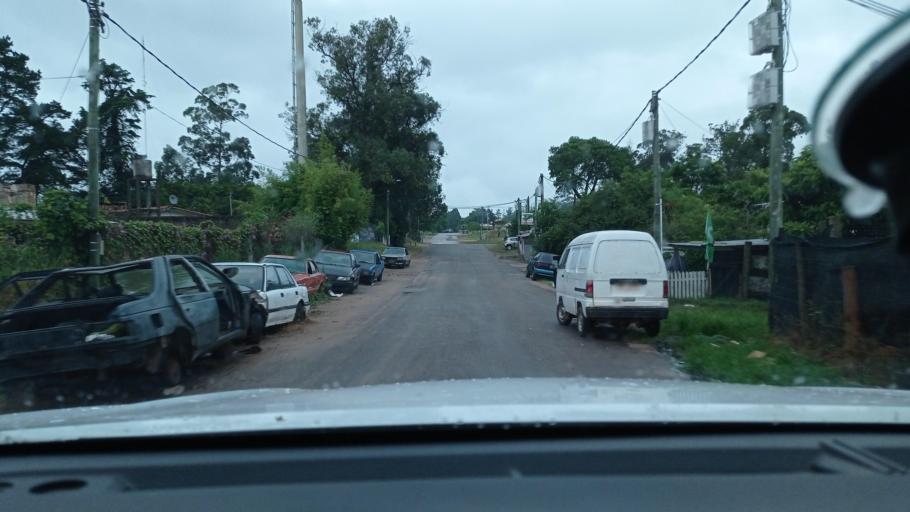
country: UY
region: Maldonado
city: Maldonado
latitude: -34.9229
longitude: -54.9120
